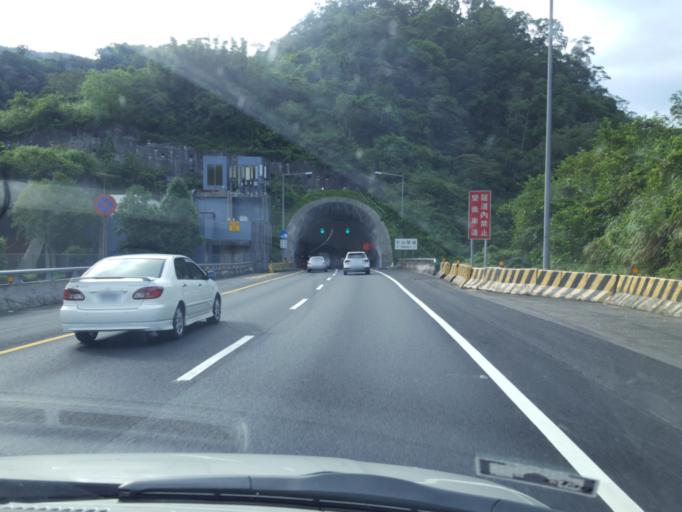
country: TW
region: Taiwan
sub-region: Keelung
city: Keelung
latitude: 24.9495
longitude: 121.7019
